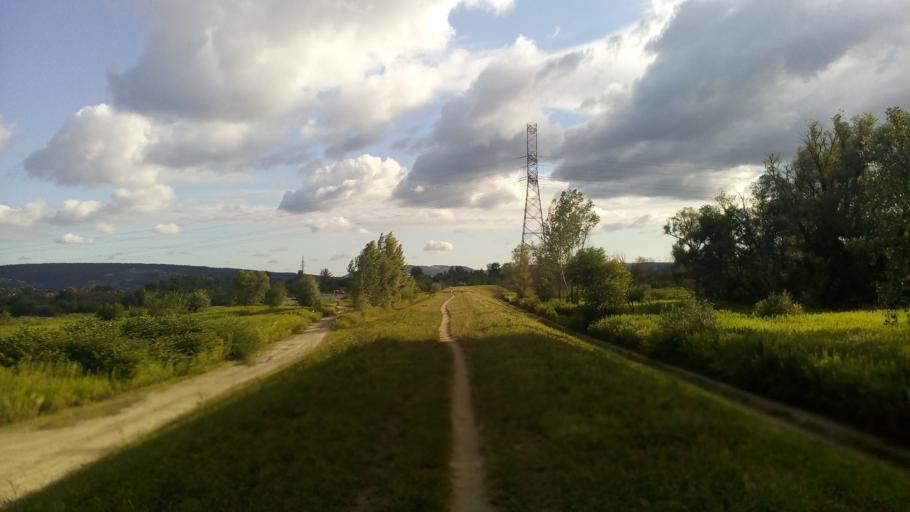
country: PL
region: Lesser Poland Voivodeship
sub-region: Powiat nowosadecki
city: Stary Sacz
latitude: 49.5929
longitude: 20.6550
